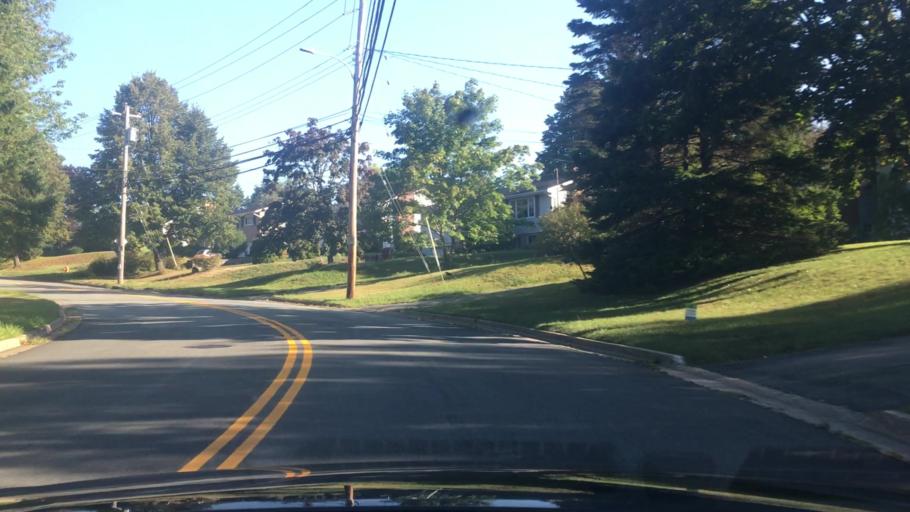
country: CA
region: Nova Scotia
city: Dartmouth
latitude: 44.7393
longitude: -63.6526
